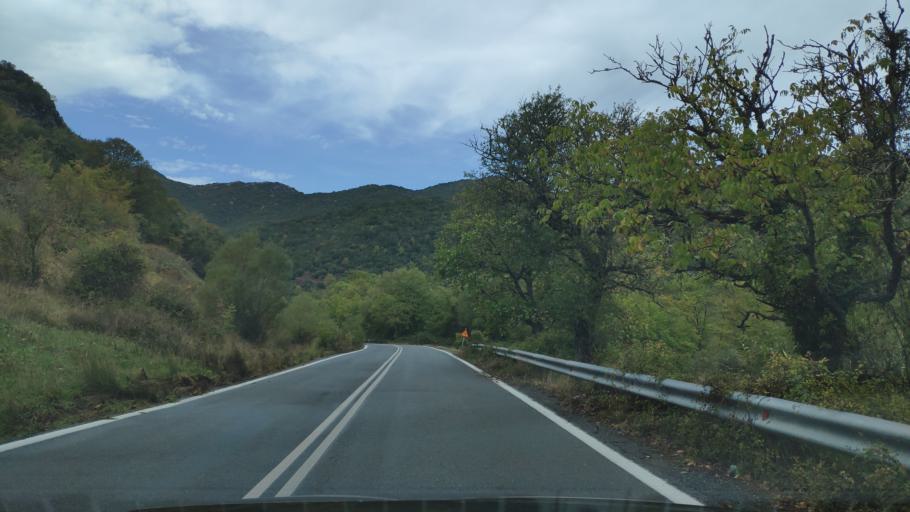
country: GR
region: Peloponnese
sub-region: Nomos Arkadias
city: Dimitsana
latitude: 37.6216
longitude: 22.0494
